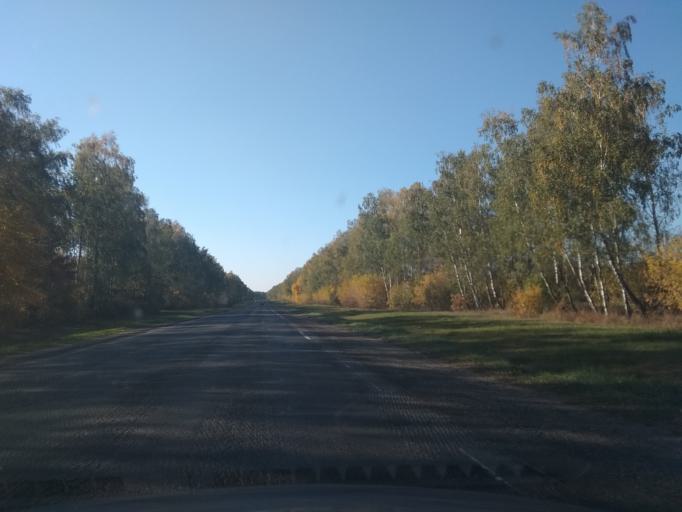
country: BY
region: Grodnenskaya
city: Zhyrovichy
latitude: 53.0580
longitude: 25.4552
